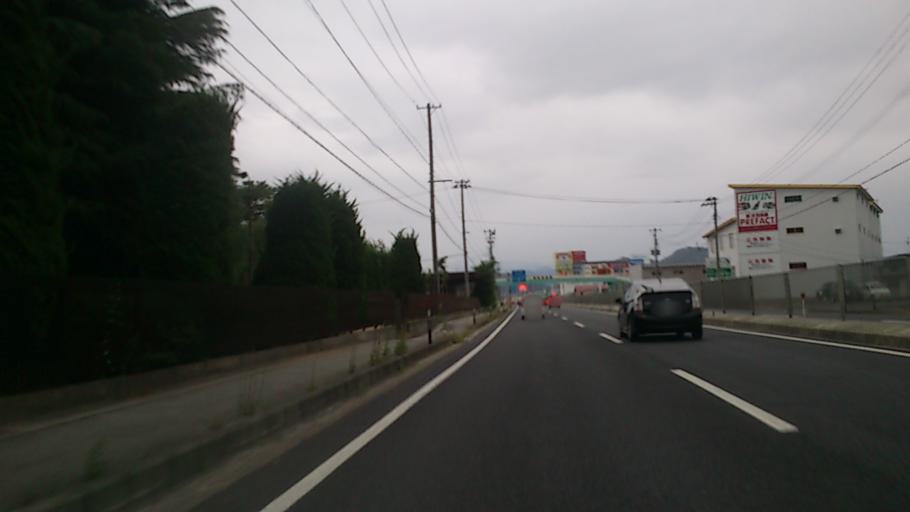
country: JP
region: Yamagata
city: Tendo
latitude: 38.3791
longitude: 140.3825
